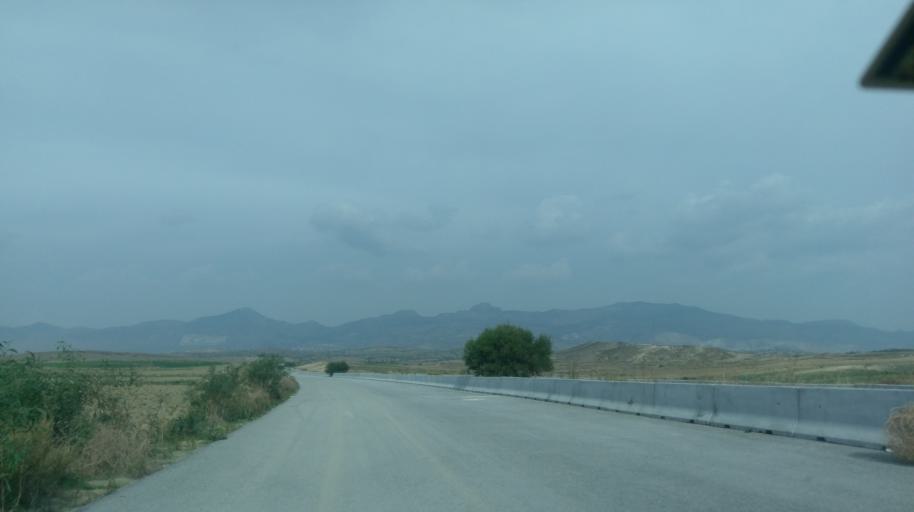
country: CY
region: Lefkosia
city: Nicosia
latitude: 35.2173
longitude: 33.4022
